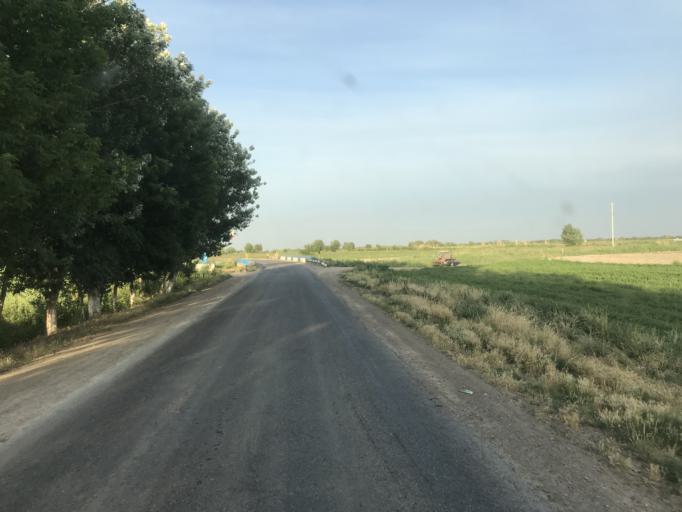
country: KZ
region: Ongtustik Qazaqstan
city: Asykata
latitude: 40.9511
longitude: 68.4523
